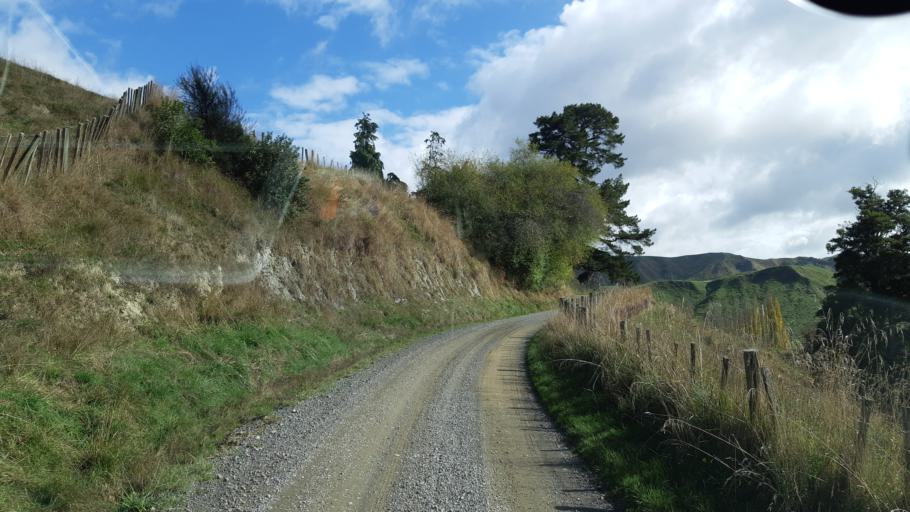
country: NZ
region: Manawatu-Wanganui
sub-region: Ruapehu District
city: Waiouru
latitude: -39.7553
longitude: 175.6636
